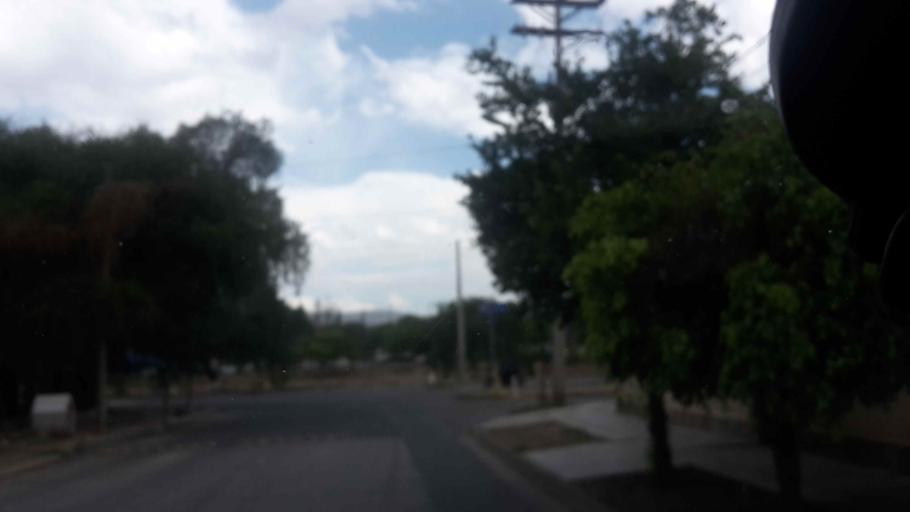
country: BO
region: Cochabamba
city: Cochabamba
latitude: -17.4040
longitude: -66.1715
